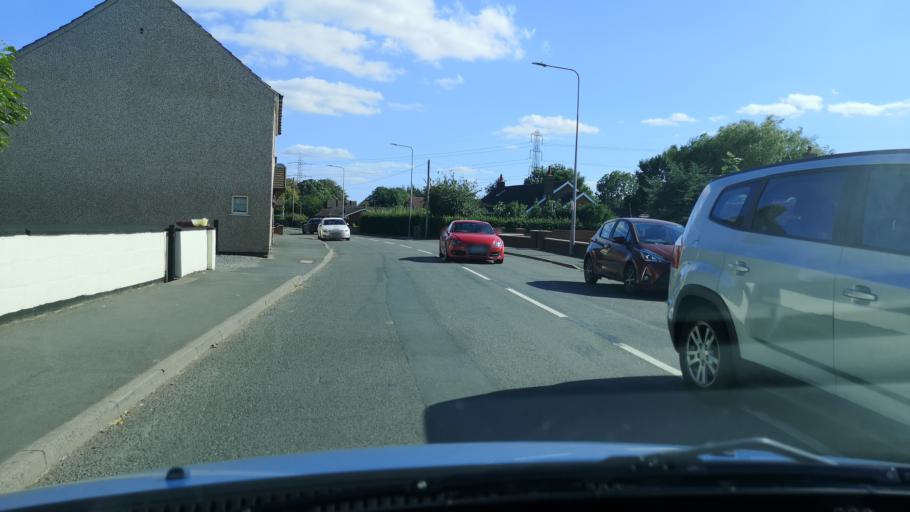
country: GB
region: England
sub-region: North Lincolnshire
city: Crowle
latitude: 53.6030
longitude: -0.8310
